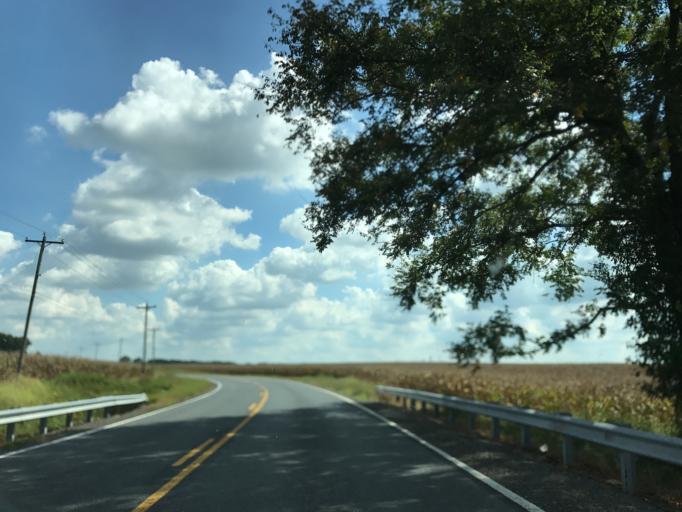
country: US
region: Maryland
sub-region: Queen Anne's County
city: Centreville
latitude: 39.0042
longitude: -75.9744
